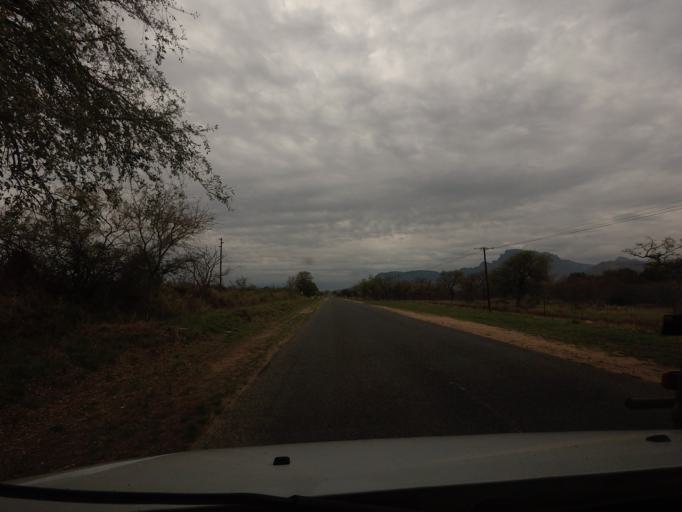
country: ZA
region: Limpopo
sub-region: Mopani District Municipality
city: Hoedspruit
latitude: -24.4557
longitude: 30.8656
